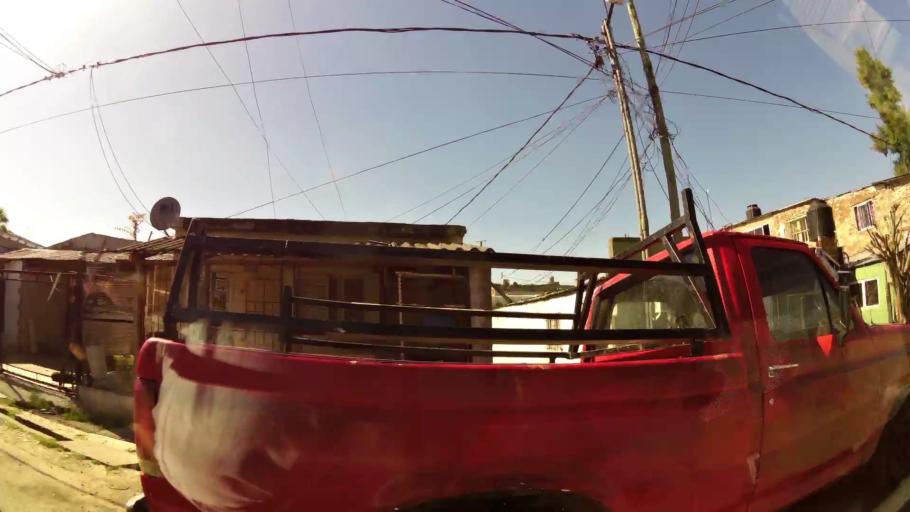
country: AR
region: Buenos Aires
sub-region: Partido de Quilmes
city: Quilmes
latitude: -34.7084
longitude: -58.3021
